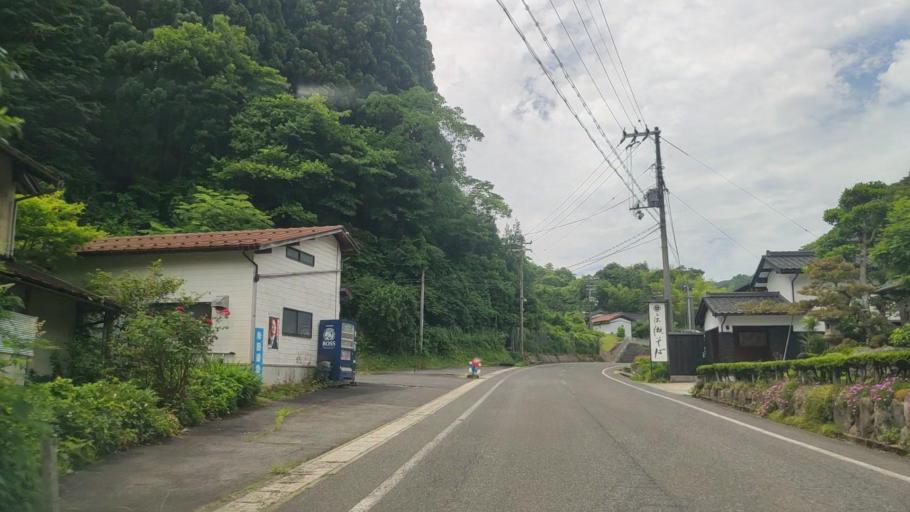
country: JP
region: Hyogo
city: Toyooka
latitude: 35.5255
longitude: 134.7055
